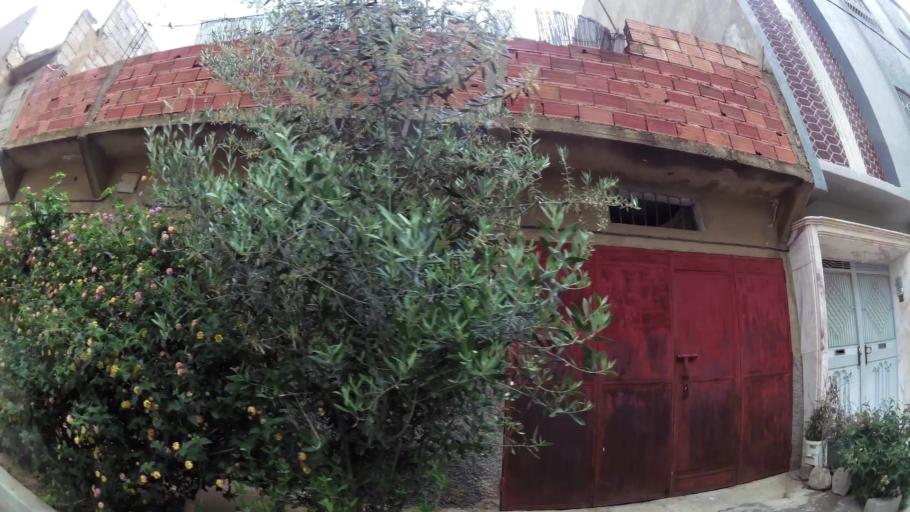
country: MA
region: Rabat-Sale-Zemmour-Zaer
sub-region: Khemisset
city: Tiflet
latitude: 33.8912
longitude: -6.3328
